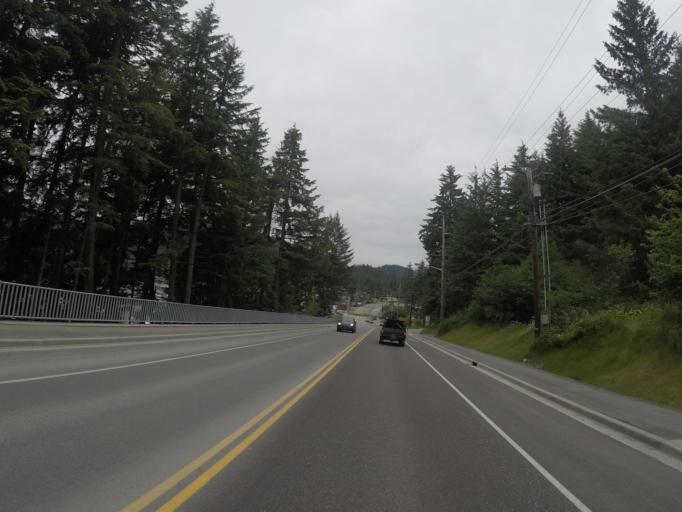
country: US
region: Alaska
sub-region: Juneau City and Borough
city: Juneau
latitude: 58.3842
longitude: -134.6444
